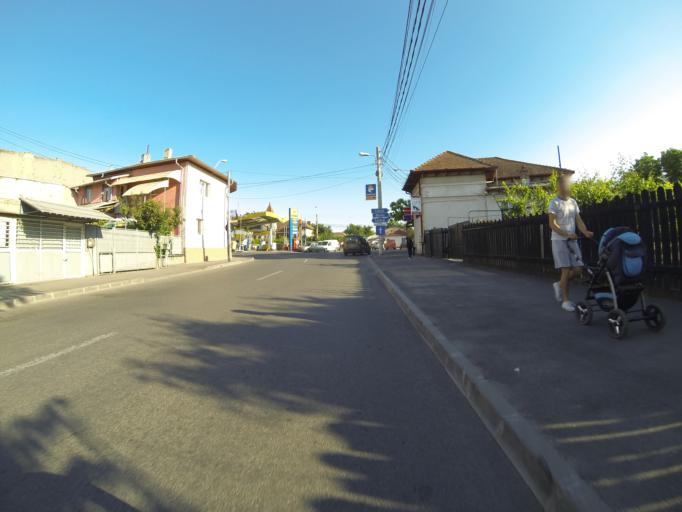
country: RO
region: Dolj
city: Craiova
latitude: 44.3077
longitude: 23.8052
